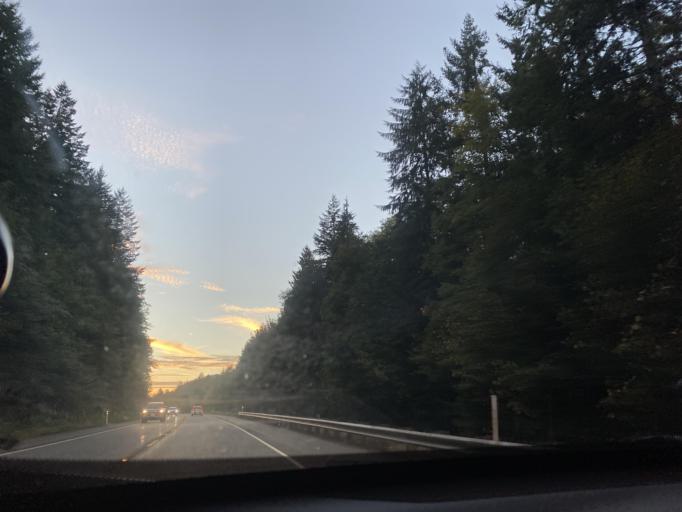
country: US
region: Washington
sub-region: Clallam County
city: Port Angeles
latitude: 48.0710
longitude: -123.6343
